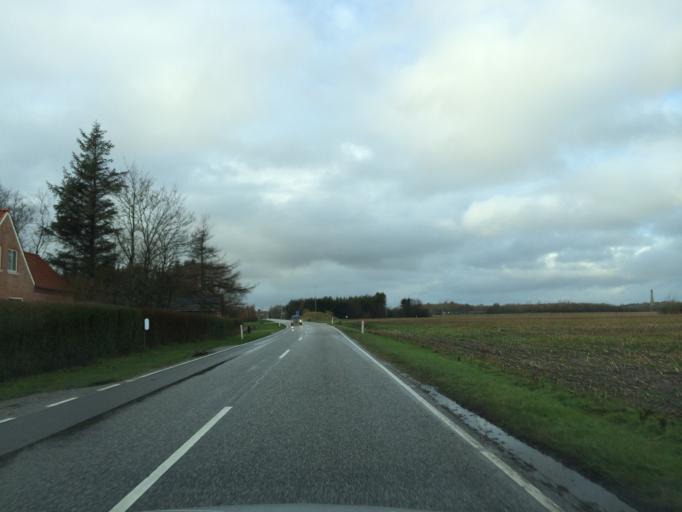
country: DK
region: Central Jutland
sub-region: Holstebro Kommune
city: Ulfborg
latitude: 56.1955
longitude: 8.3207
